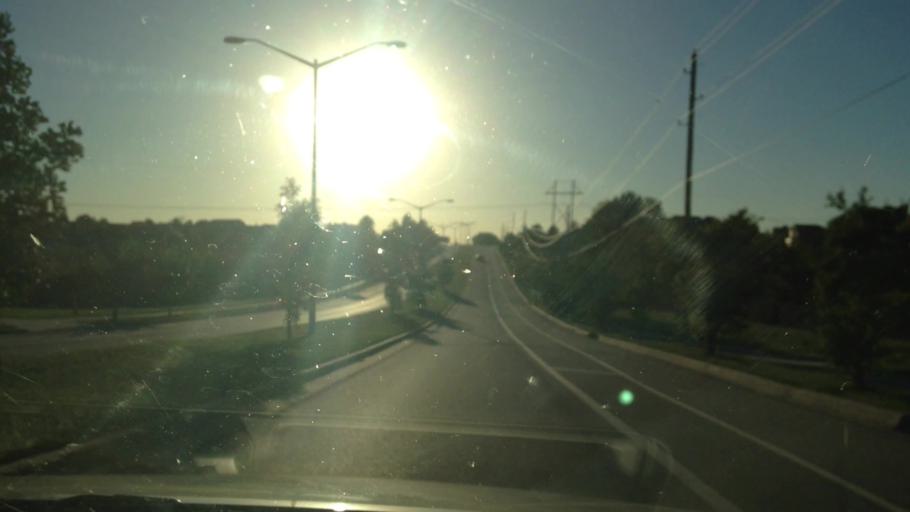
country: US
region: Missouri
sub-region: Clay County
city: Pleasant Valley
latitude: 39.2885
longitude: -94.4805
